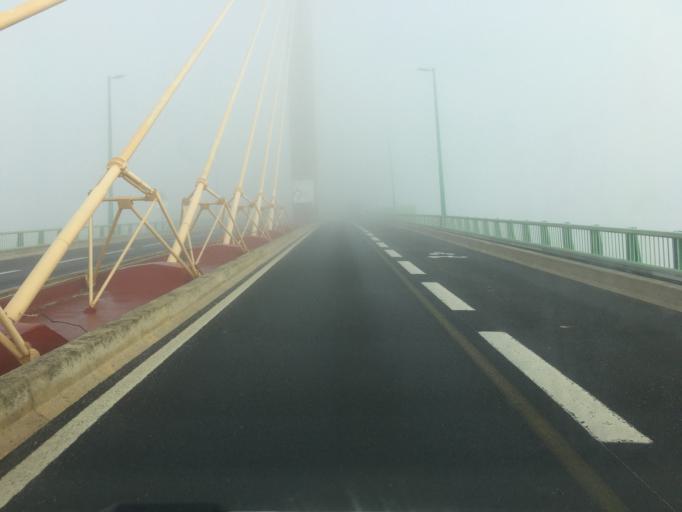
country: FR
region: Haute-Normandie
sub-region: Departement de la Seine-Maritime
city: Saint-Wandrille-Rancon
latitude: 49.5216
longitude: 0.7481
